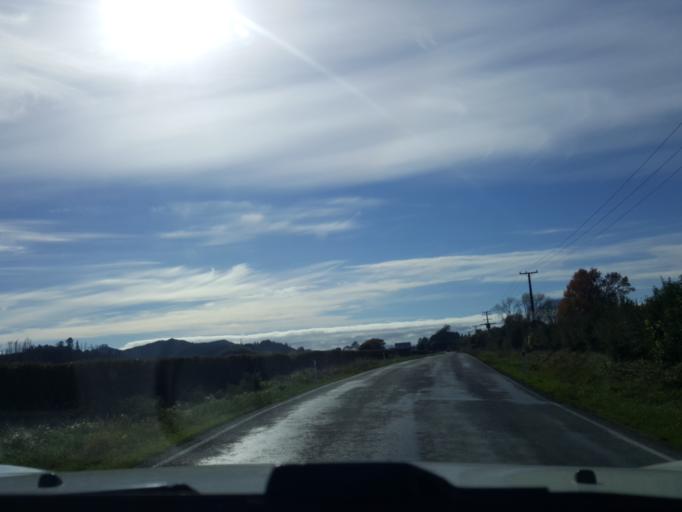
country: NZ
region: Waikato
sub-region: Waikato District
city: Ngaruawahia
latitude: -37.6056
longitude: 175.1984
